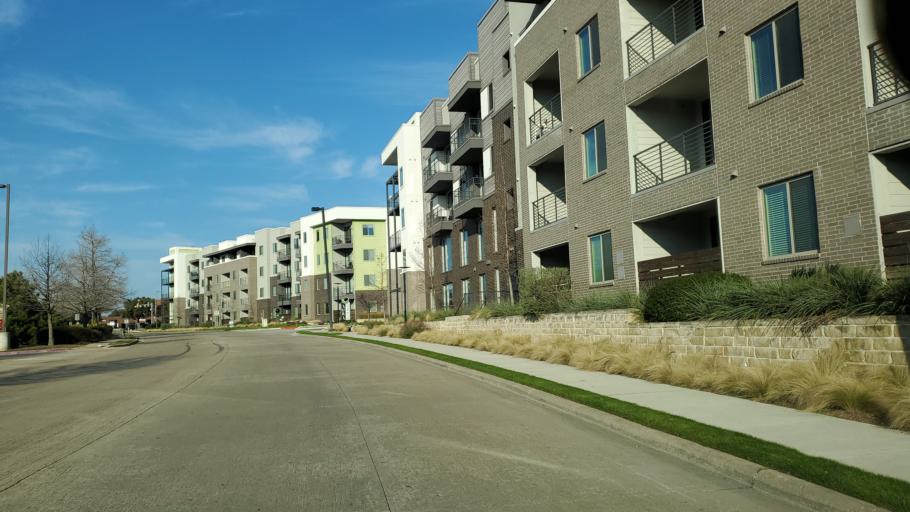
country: US
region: Texas
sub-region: Collin County
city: Plano
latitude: 33.0057
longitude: -96.7034
